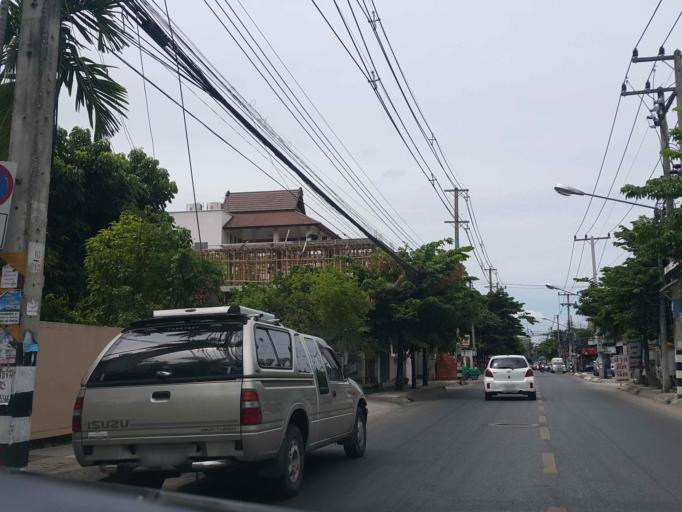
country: TH
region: Chiang Mai
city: Chiang Mai
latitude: 18.7773
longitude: 98.9810
